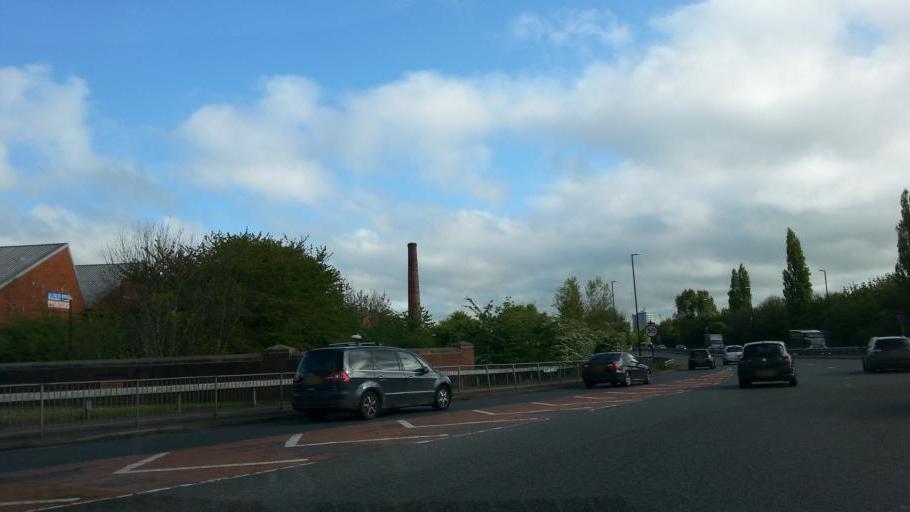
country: GB
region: England
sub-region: Coventry
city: Coventry
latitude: 52.4224
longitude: -1.4873
